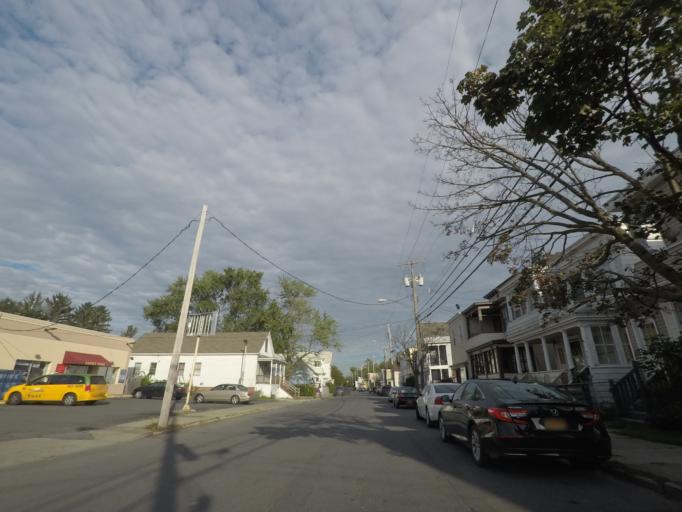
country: US
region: New York
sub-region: Albany County
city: Albany
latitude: 42.6390
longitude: -73.7762
